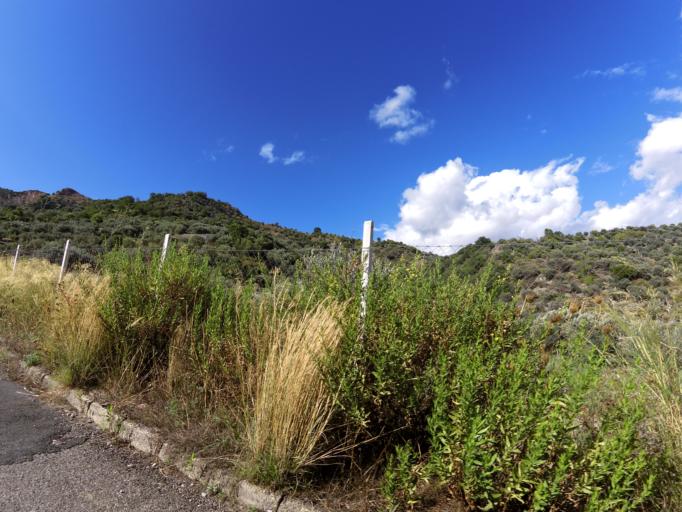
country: IT
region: Calabria
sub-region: Provincia di Reggio Calabria
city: Bivongi
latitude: 38.4894
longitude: 16.4578
